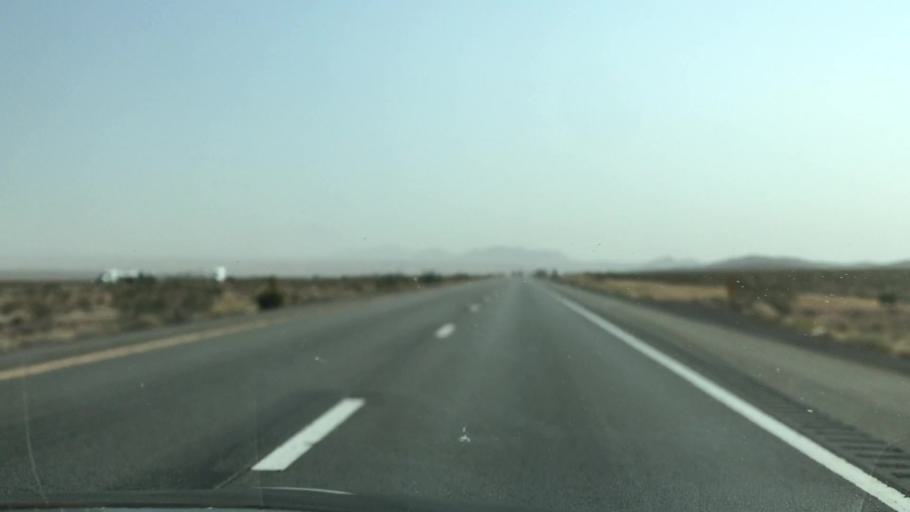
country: US
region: Nevada
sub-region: Clark County
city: Moapa Town
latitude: 36.6237
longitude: -114.6136
